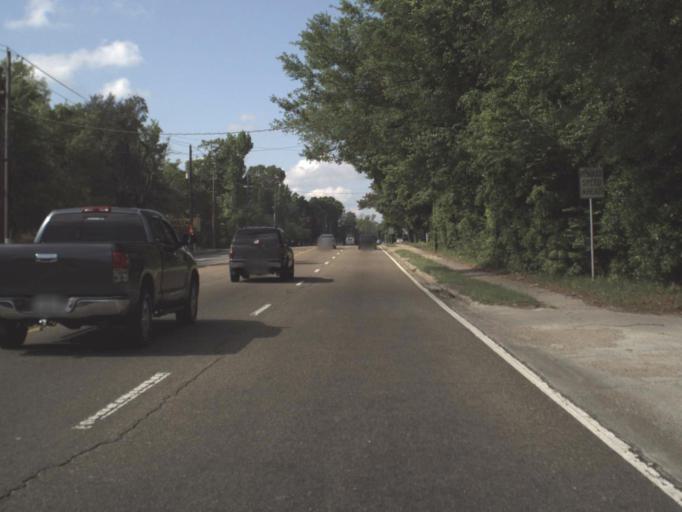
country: US
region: Florida
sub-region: Escambia County
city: Ferry Pass
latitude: 30.5222
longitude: -87.2124
